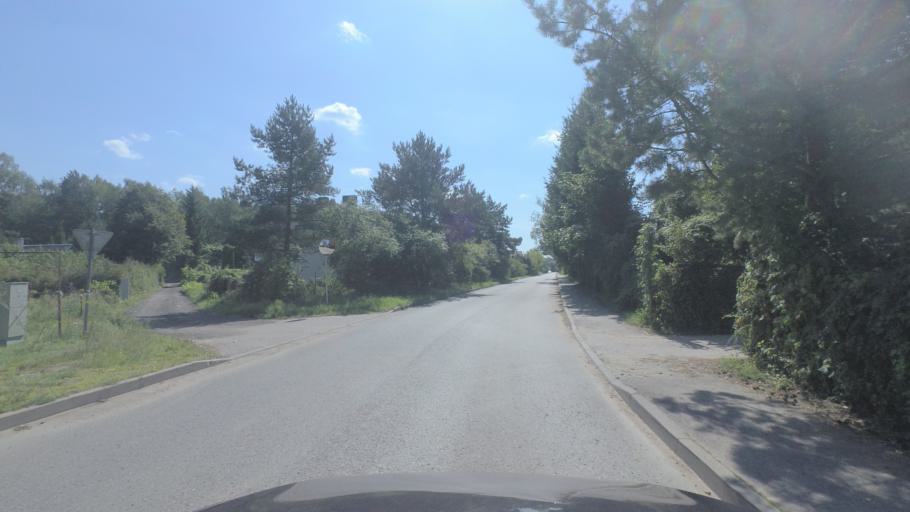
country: LT
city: Nemencine
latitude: 54.8367
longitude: 25.3706
